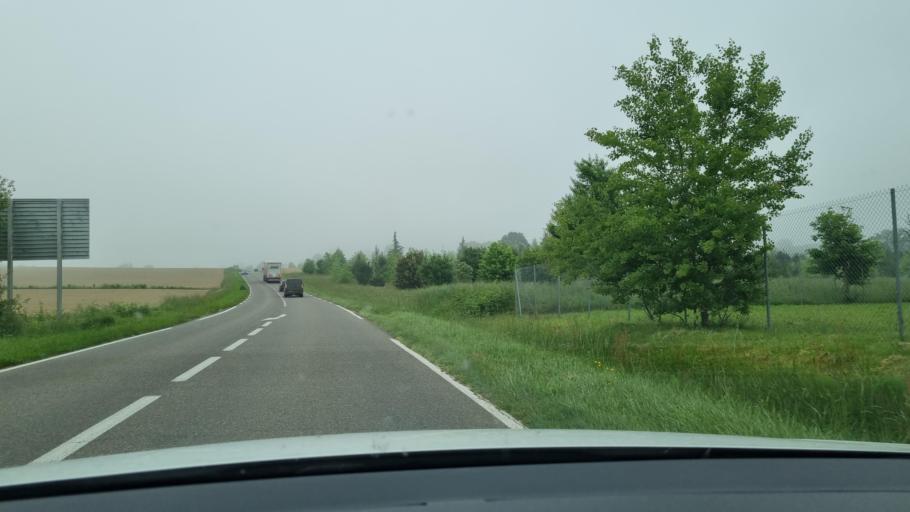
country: FR
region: Aquitaine
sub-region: Departement des Landes
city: Hagetmau
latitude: 43.6653
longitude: -0.6008
